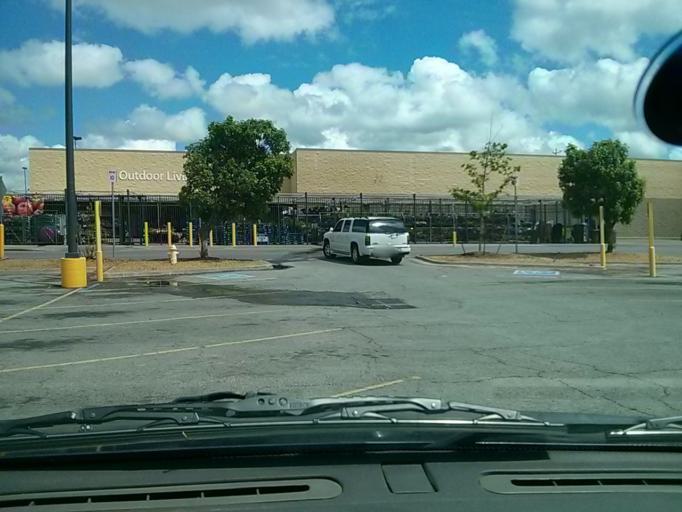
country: US
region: Oklahoma
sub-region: Tulsa County
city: Tulsa
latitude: 36.1602
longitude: -95.8844
